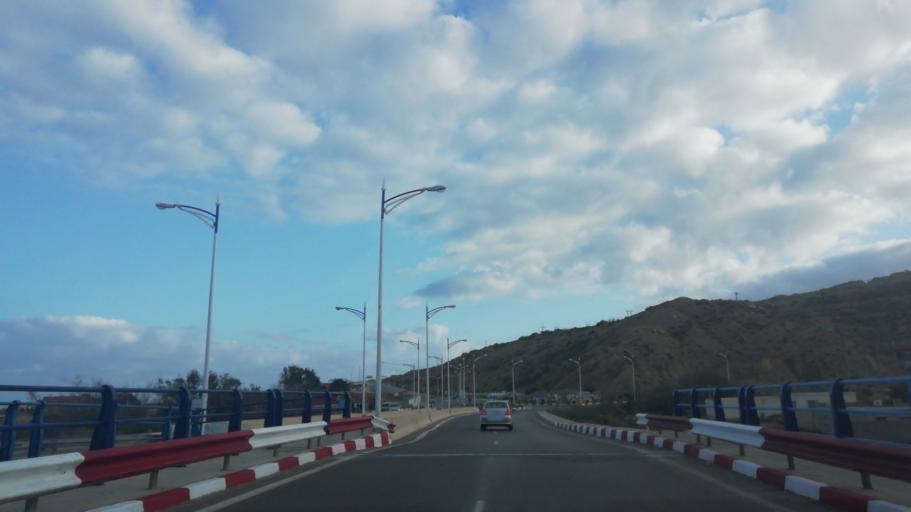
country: DZ
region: Mostaganem
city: Mostaganem
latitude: 36.0349
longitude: 0.1417
